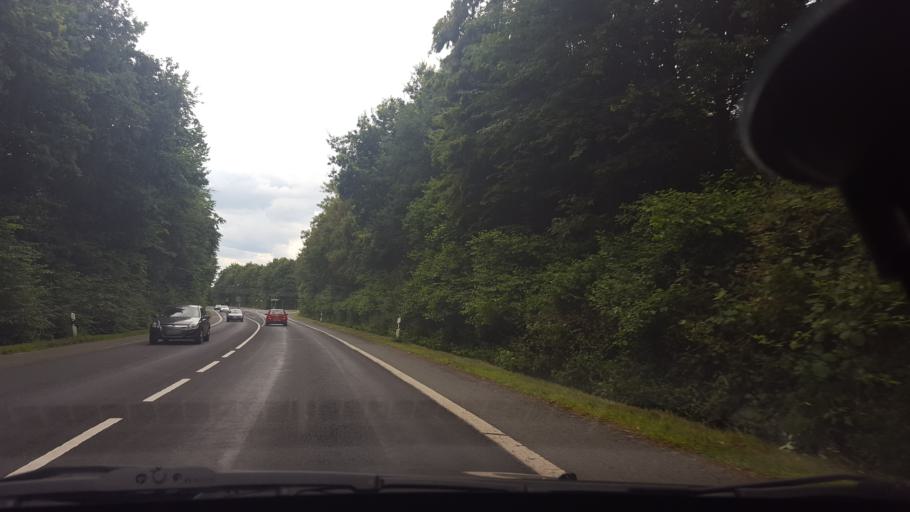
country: DE
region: North Rhine-Westphalia
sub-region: Regierungsbezirk Munster
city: Recklinghausen
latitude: 51.6161
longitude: 7.2194
